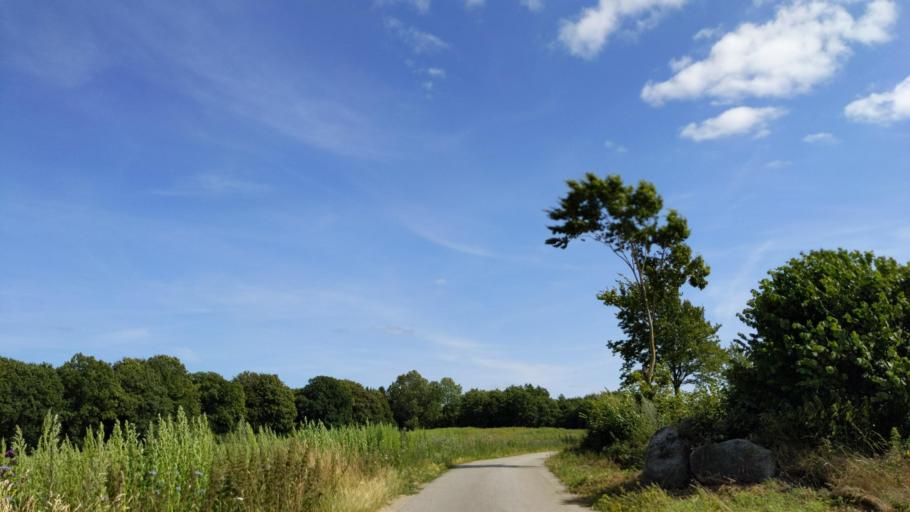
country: DE
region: Schleswig-Holstein
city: Kasseedorf
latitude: 54.1260
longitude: 10.7427
